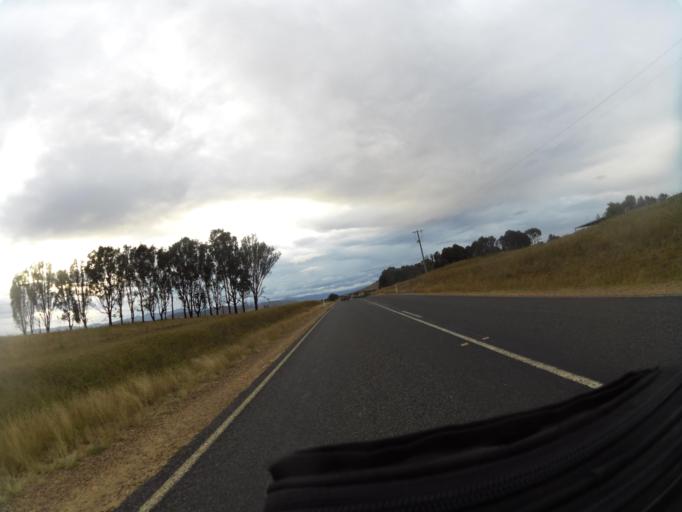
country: AU
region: New South Wales
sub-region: Greater Hume Shire
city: Holbrook
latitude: -36.0587
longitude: 147.9433
